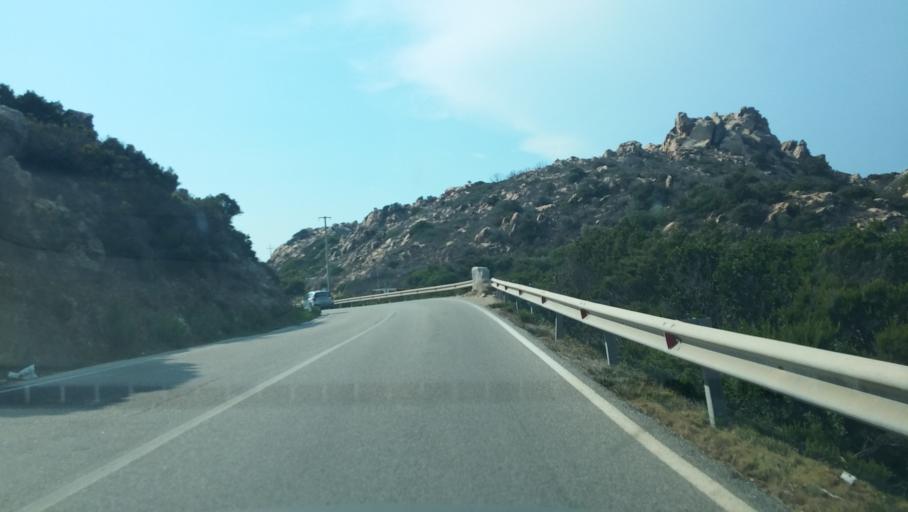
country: IT
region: Sardinia
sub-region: Provincia di Olbia-Tempio
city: La Maddalena
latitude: 41.2572
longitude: 9.4245
